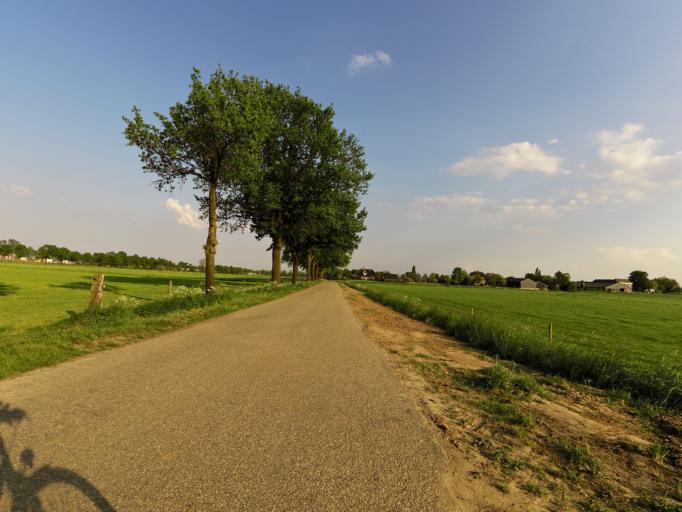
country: NL
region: Gelderland
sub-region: Oude IJsselstreek
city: Gendringen
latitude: 51.8946
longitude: 6.3558
